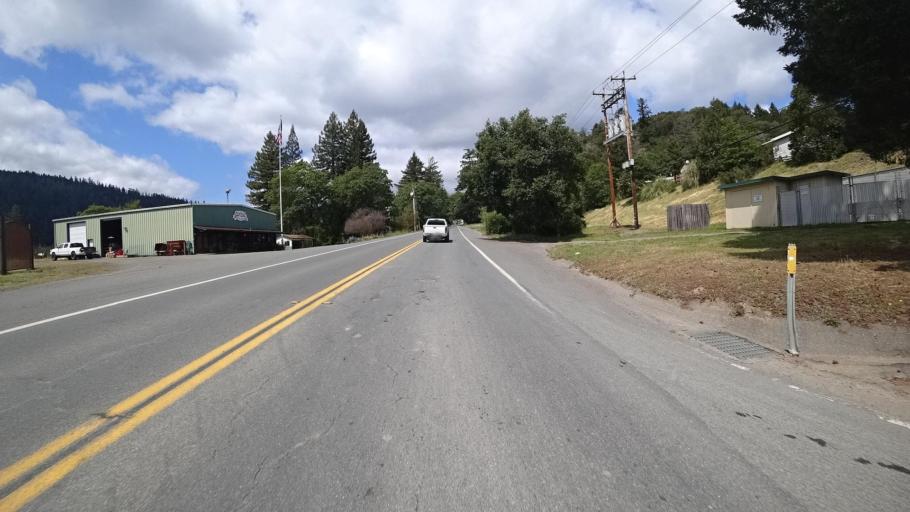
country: US
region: California
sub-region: Humboldt County
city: Redway
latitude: 40.1154
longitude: -123.8144
